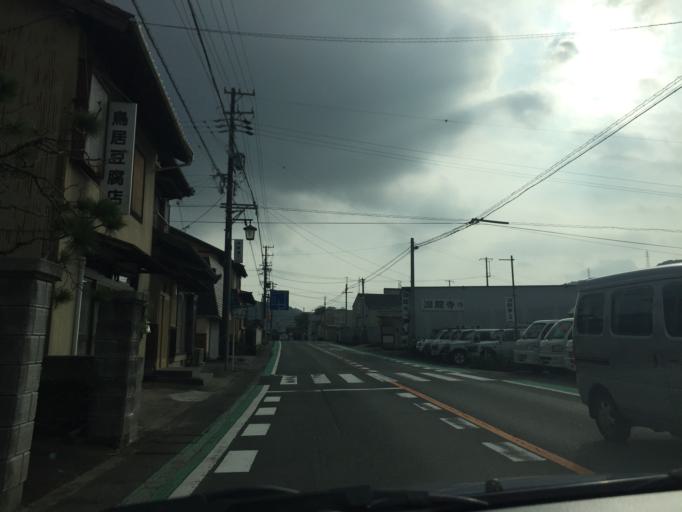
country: JP
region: Aichi
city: Shinshiro
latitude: 34.9516
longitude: 137.6065
